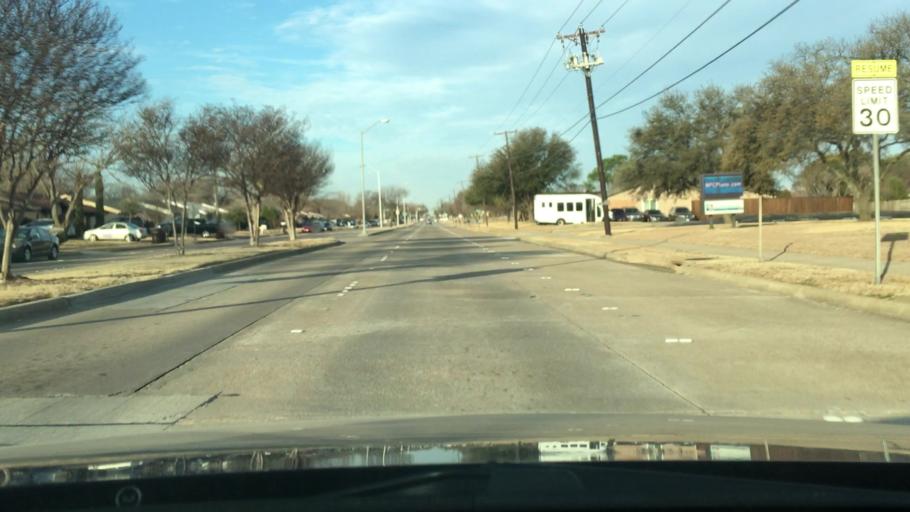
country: US
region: Texas
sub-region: Collin County
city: Plano
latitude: 33.0313
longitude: -96.6858
